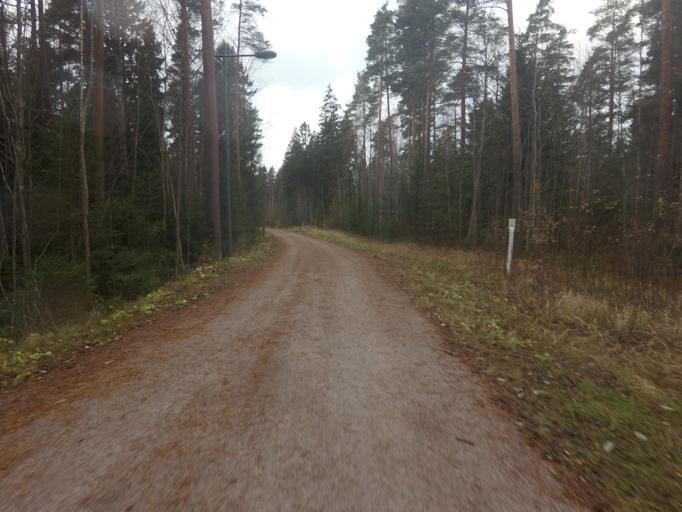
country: FI
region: Uusimaa
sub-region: Helsinki
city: Kauniainen
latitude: 60.1831
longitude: 24.7027
